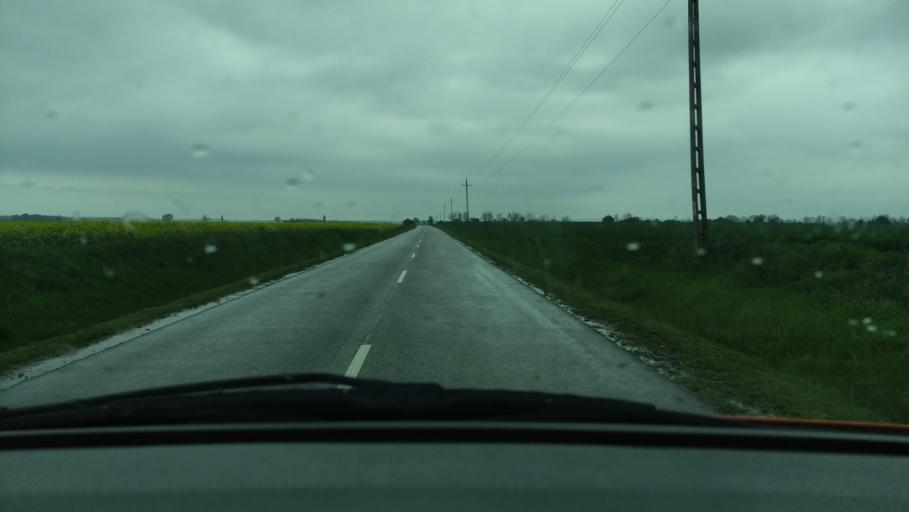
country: HU
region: Baranya
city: Mohacs
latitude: 45.9492
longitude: 18.6834
